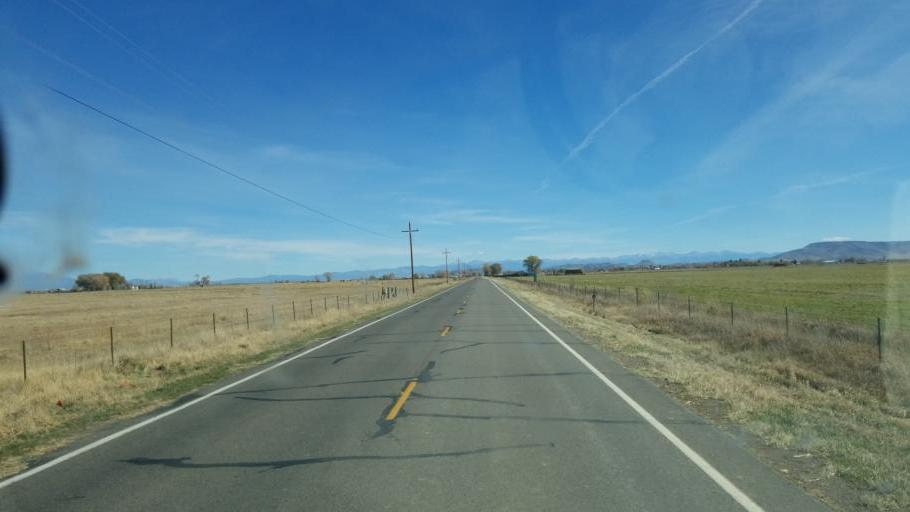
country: US
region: Colorado
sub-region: Conejos County
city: Conejos
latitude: 37.2836
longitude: -105.9965
